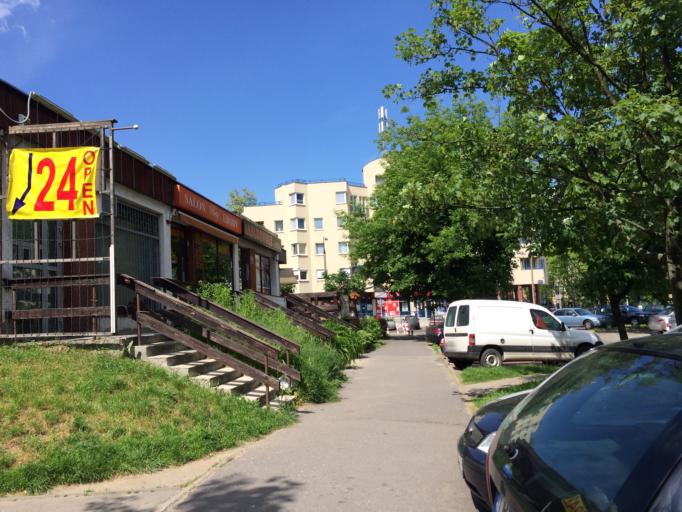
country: PL
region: Masovian Voivodeship
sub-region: Warszawa
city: Praga Poludnie
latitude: 52.2368
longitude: 21.1035
